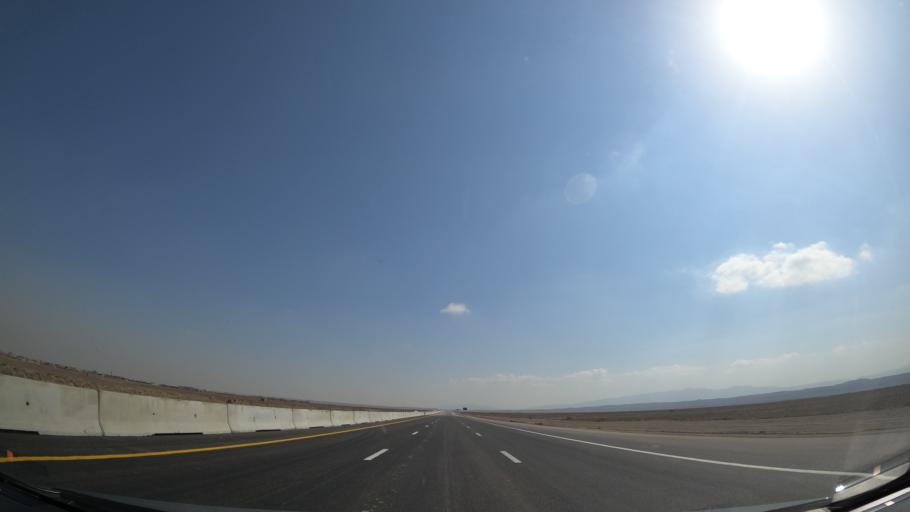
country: IR
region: Alborz
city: Nazarabad
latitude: 35.8413
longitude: 50.4862
